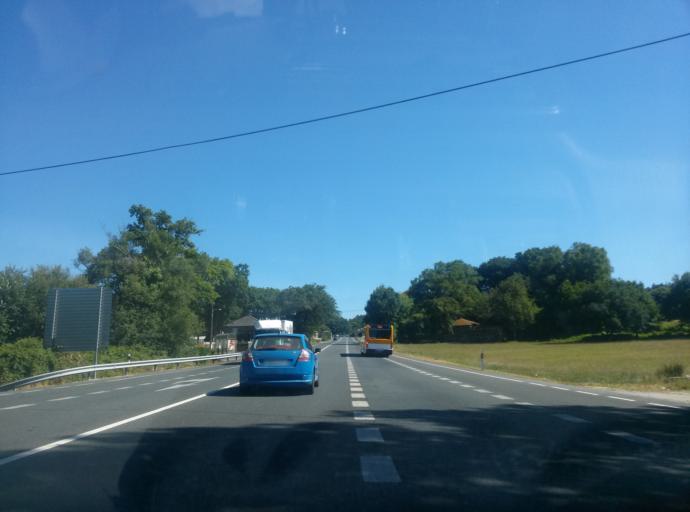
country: ES
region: Galicia
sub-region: Provincia de Lugo
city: Outeiro de Rei
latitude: 43.0570
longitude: -7.5980
